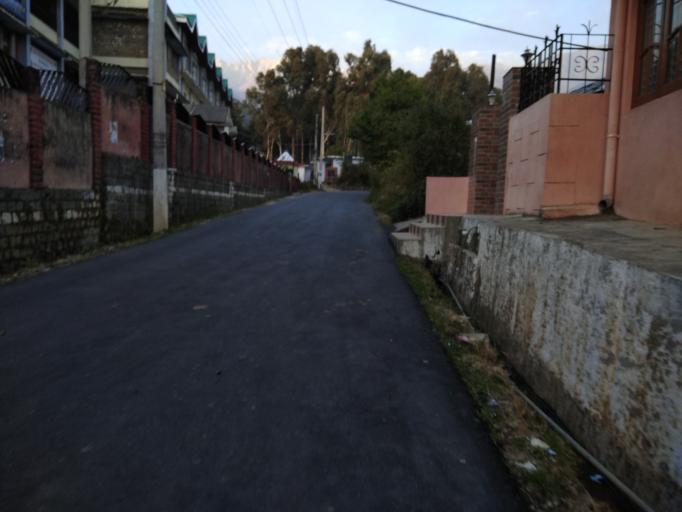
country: IN
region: Himachal Pradesh
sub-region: Kangra
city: Palampur
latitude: 32.1229
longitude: 76.5274
